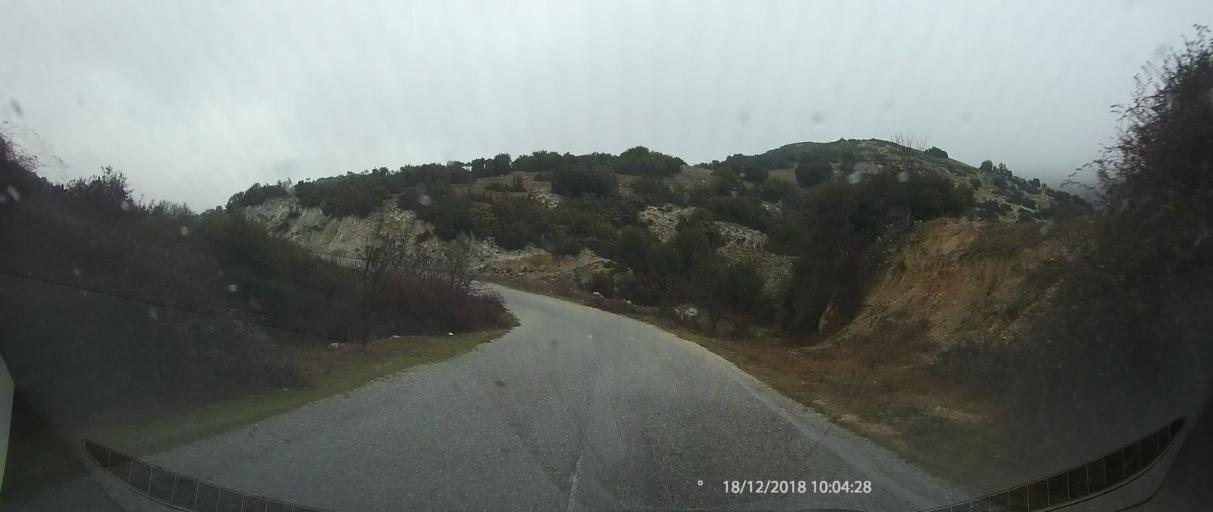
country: GR
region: Thessaly
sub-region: Nomos Larisis
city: Livadi
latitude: 40.0530
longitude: 22.2225
